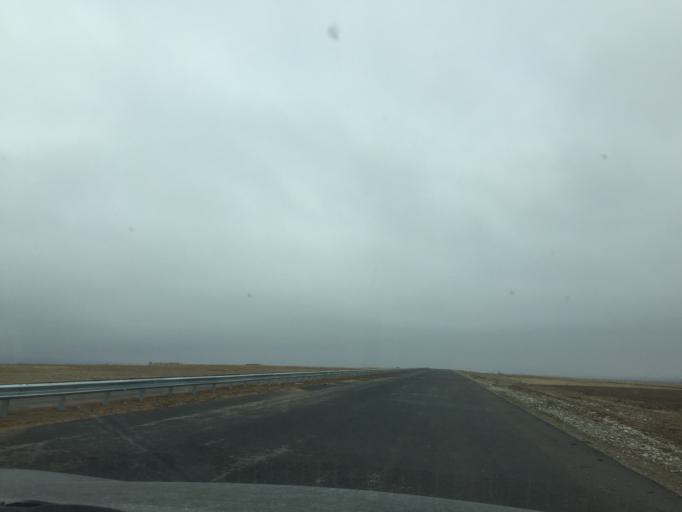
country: KZ
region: Ongtustik Qazaqstan
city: Kokterek
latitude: 42.5426
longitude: 70.2791
